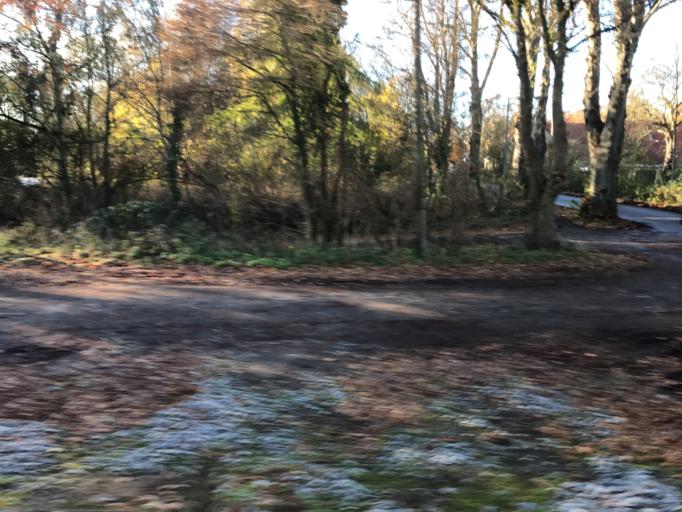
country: DK
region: Zealand
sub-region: Stevns Kommune
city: Stroby Egede
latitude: 55.4007
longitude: 12.1922
